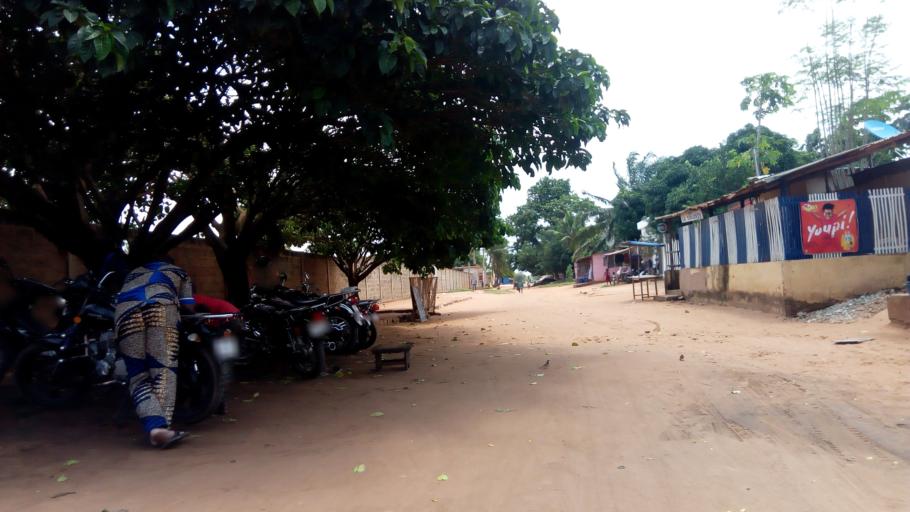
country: TG
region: Maritime
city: Lome
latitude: 6.1848
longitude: 1.1777
